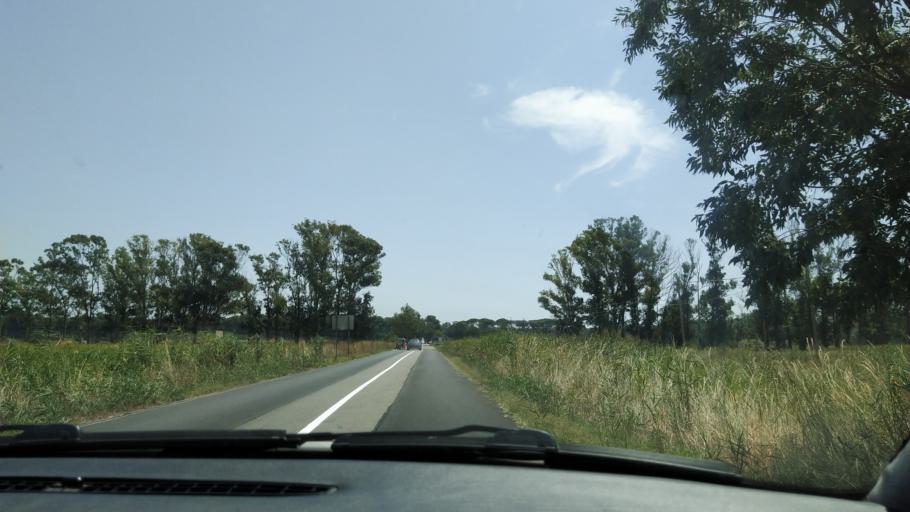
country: IT
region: Basilicate
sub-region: Provincia di Matera
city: Marconia
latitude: 40.3263
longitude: 16.7896
